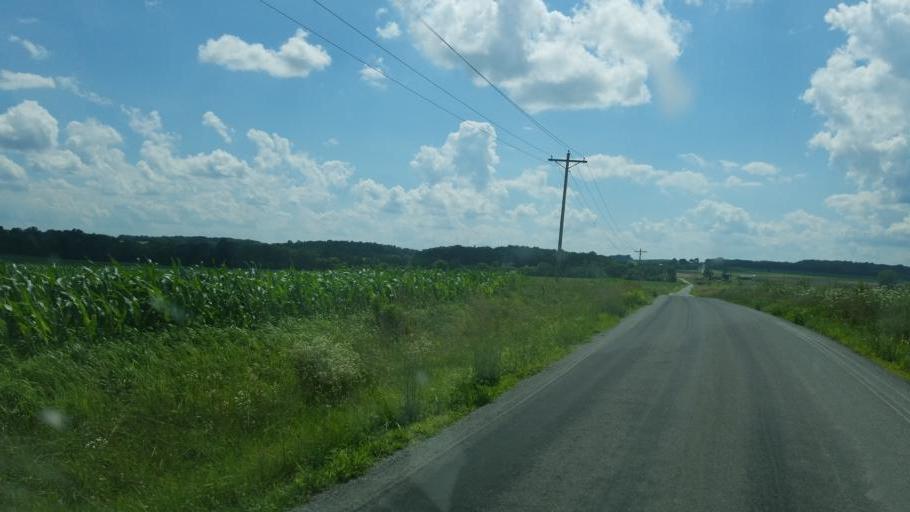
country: US
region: Ohio
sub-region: Highland County
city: Greenfield
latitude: 39.2478
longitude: -83.4244
